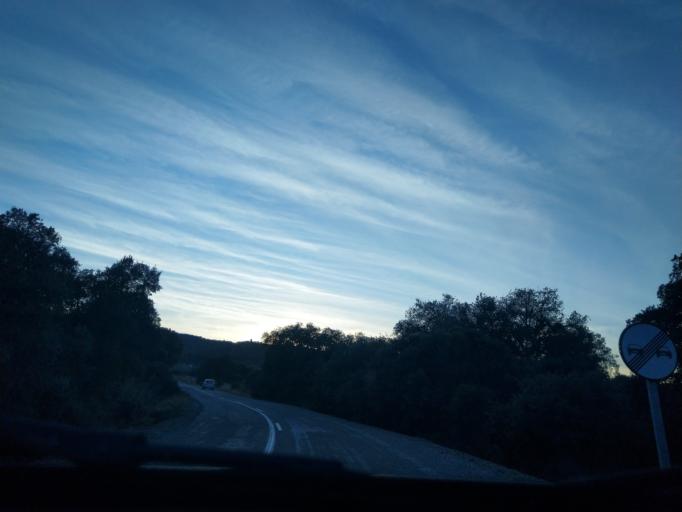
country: ES
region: Extremadura
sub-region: Provincia de Badajoz
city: Reina
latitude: 38.1657
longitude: -5.8926
